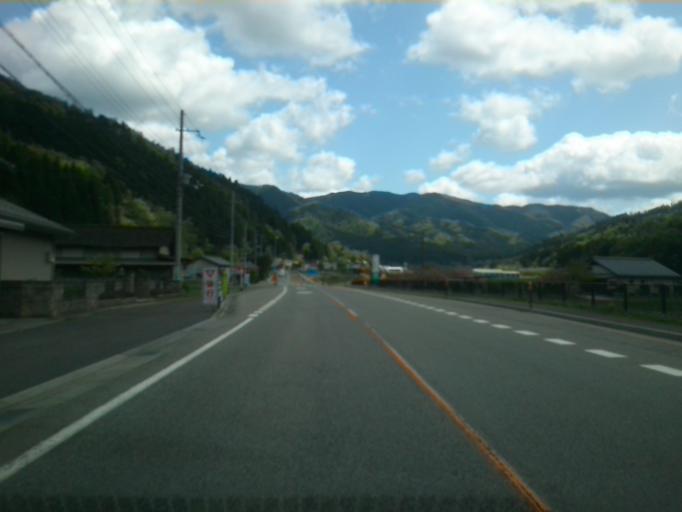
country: JP
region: Kyoto
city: Fukuchiyama
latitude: 35.4271
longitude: 135.0055
